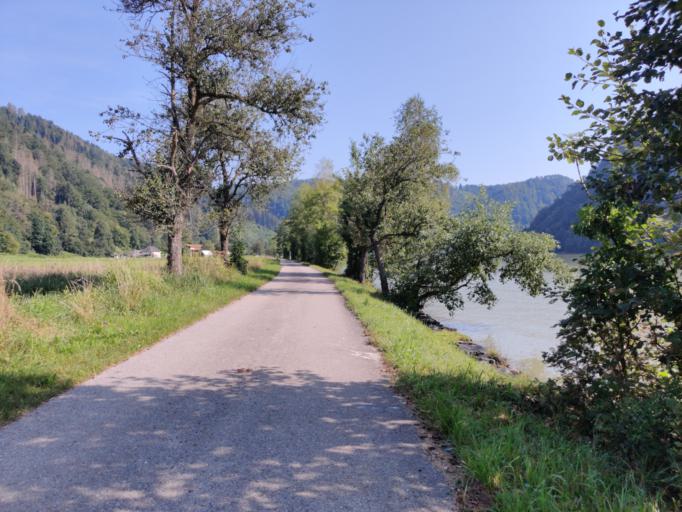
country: AT
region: Upper Austria
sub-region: Politischer Bezirk Rohrbach
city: Kleinzell im Muehlkreis
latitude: 48.4092
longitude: 13.9499
